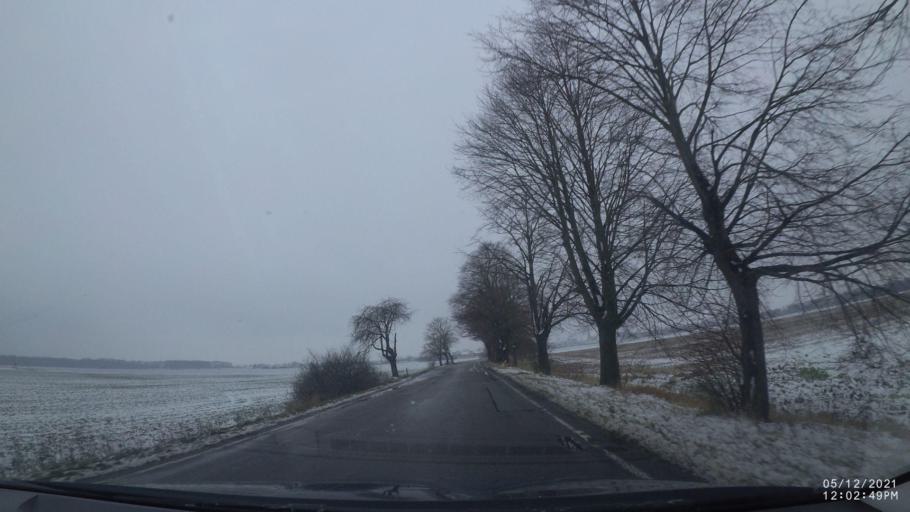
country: CZ
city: Ceske Mezirici
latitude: 50.2799
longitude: 16.0715
